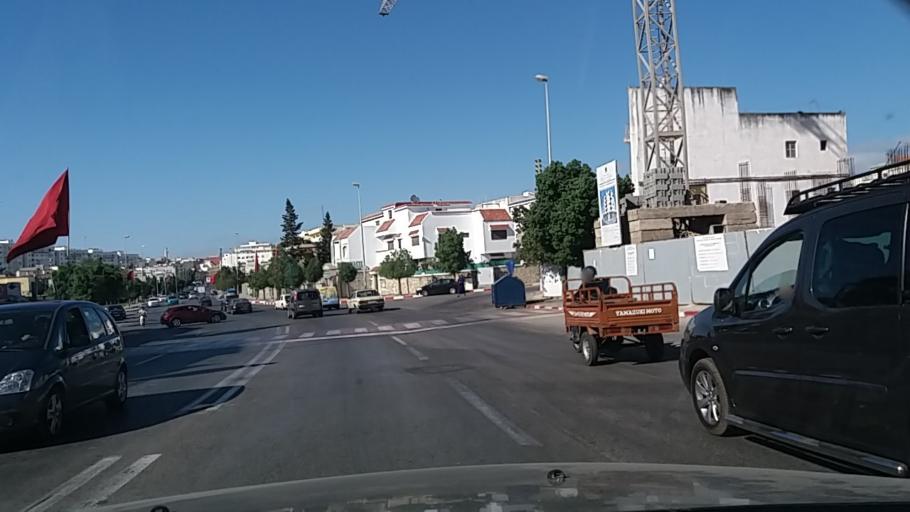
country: MA
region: Tanger-Tetouan
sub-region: Tanger-Assilah
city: Tangier
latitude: 35.7706
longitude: -5.8314
